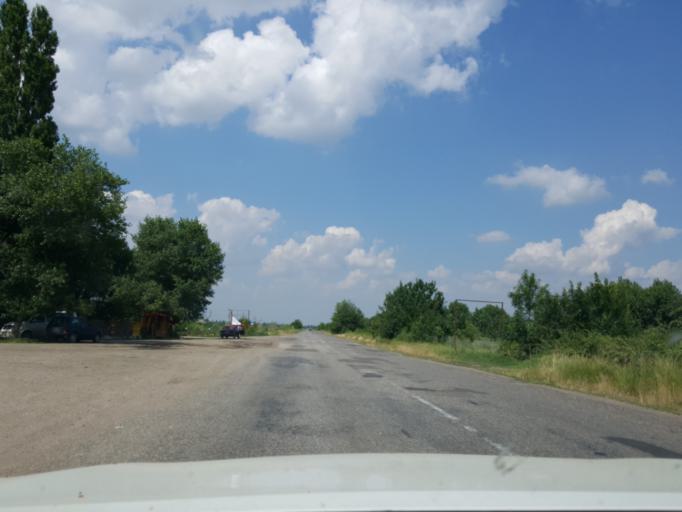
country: UA
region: Odessa
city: Starokozache
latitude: 46.3976
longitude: 30.0962
